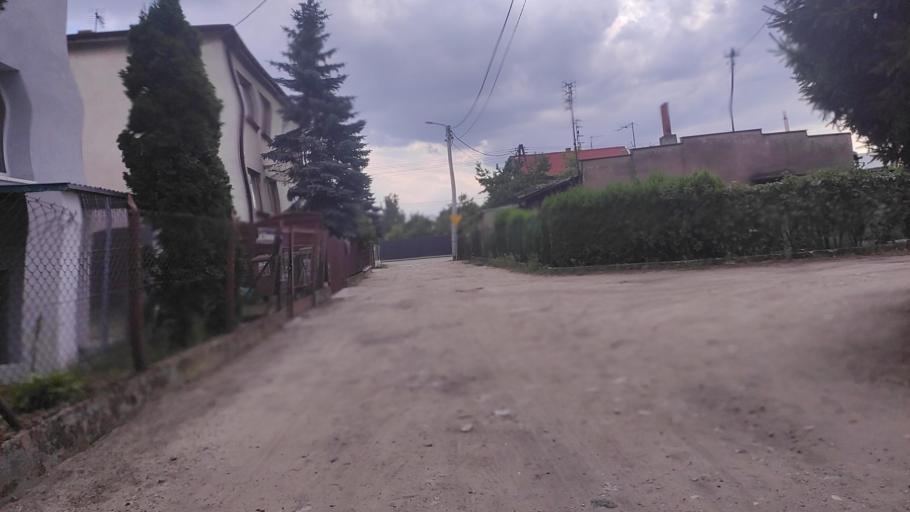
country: PL
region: Greater Poland Voivodeship
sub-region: Powiat poznanski
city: Swarzedz
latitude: 52.4036
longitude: 17.0719
